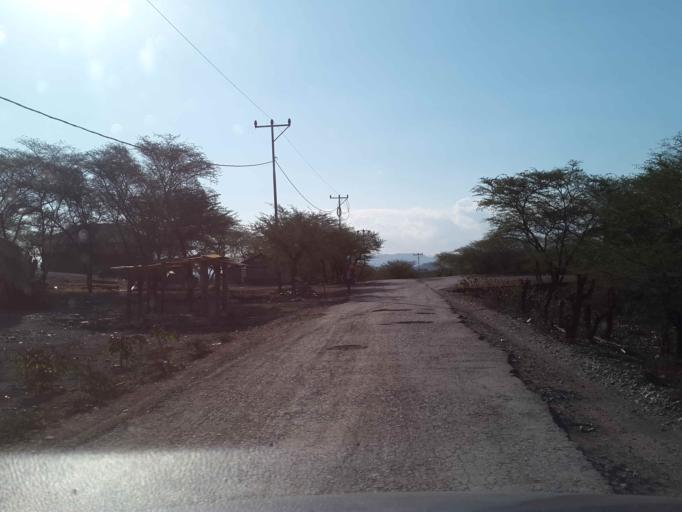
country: ID
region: East Nusa Tenggara
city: Bokong Timur
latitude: -9.9623
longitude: 124.0698
